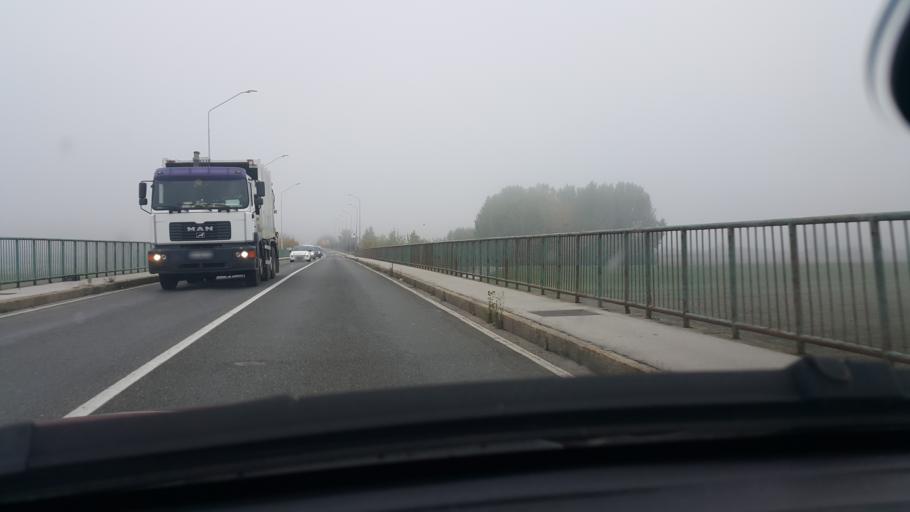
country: SI
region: Brezice
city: Brezice
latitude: 45.8947
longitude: 15.6035
